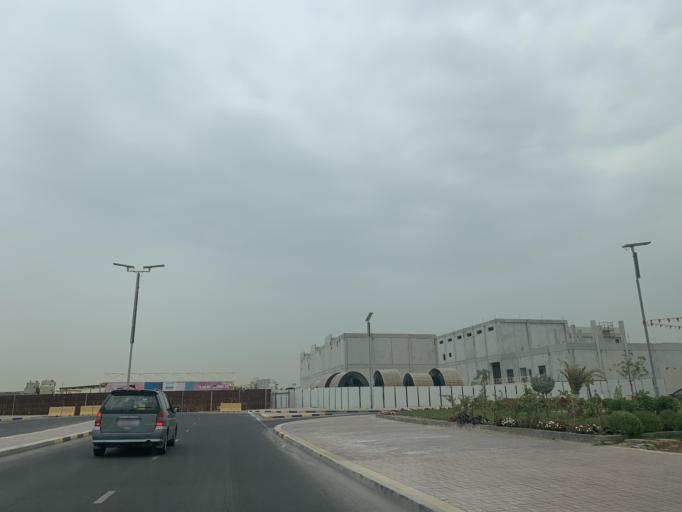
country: BH
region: Northern
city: Madinat `Isa
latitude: 26.1786
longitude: 50.5178
